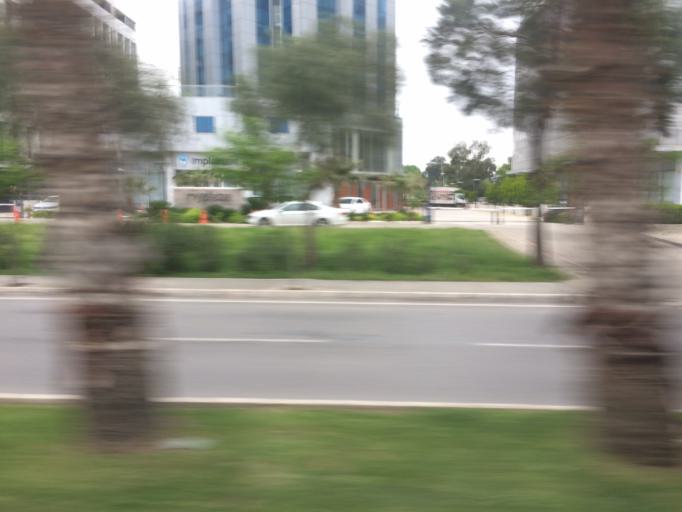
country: TR
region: Izmir
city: Izmir
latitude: 38.4569
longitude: 27.1669
